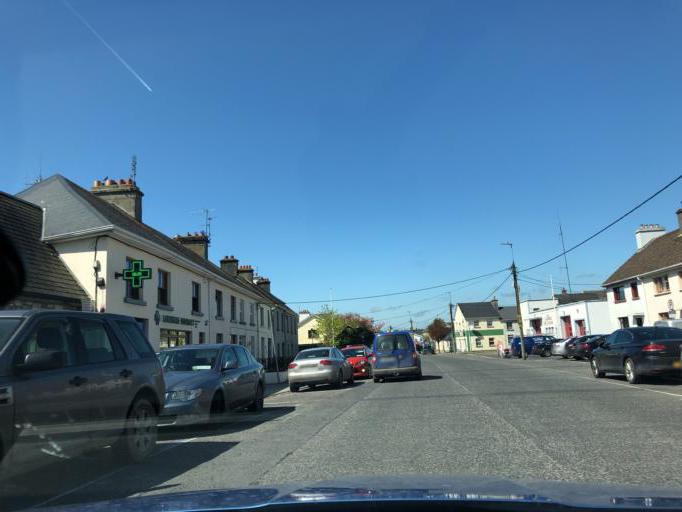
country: IE
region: Connaught
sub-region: County Galway
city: Loughrea
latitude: 53.1975
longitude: -8.5688
